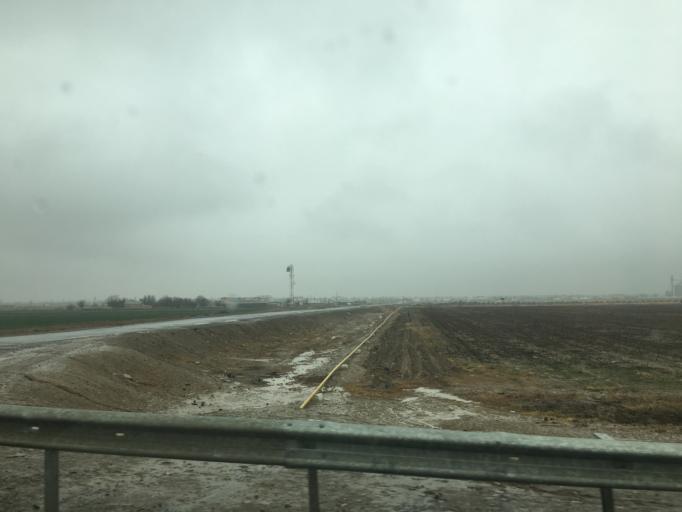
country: TM
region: Mary
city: Bayramaly
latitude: 37.4118
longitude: 62.1639
